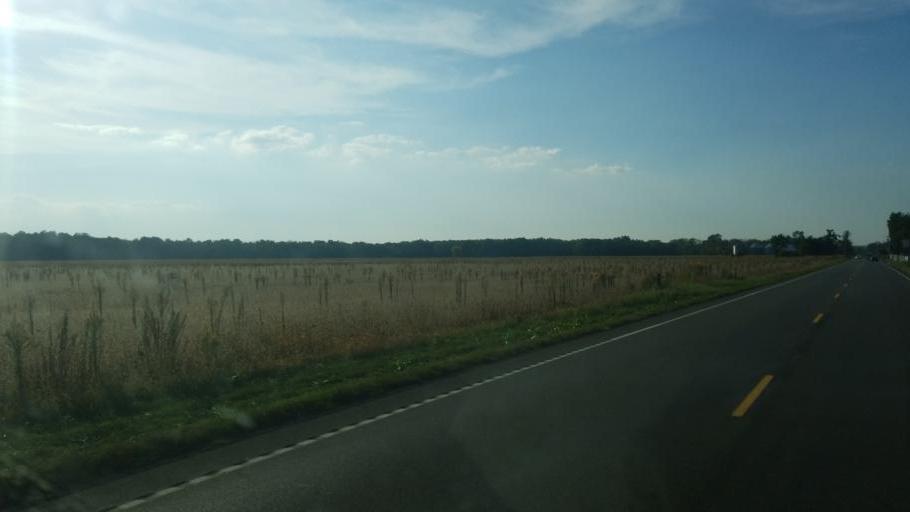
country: US
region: Ohio
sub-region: Knox County
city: Fredericktown
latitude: 40.4481
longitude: -82.5348
